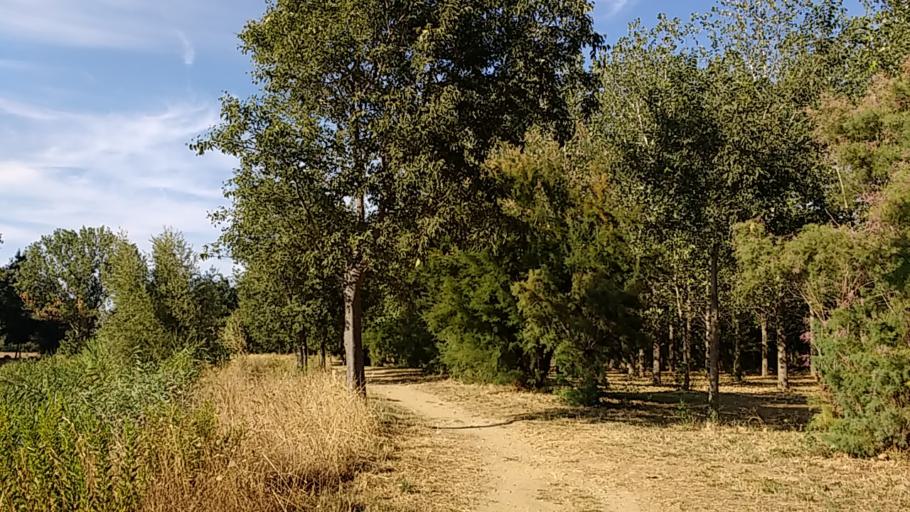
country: FR
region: Languedoc-Roussillon
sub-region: Departement des Pyrenees-Orientales
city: Palau-del-Vidre
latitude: 42.5804
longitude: 2.9610
